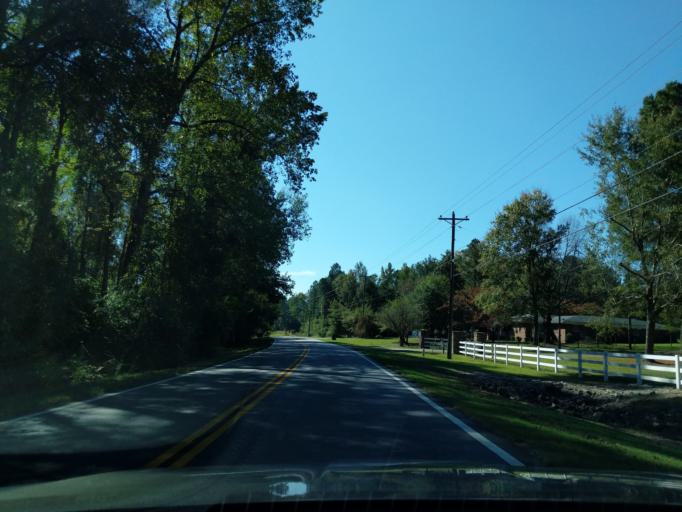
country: US
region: Georgia
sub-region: Richmond County
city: Hephzibah
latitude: 33.3169
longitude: -82.0188
